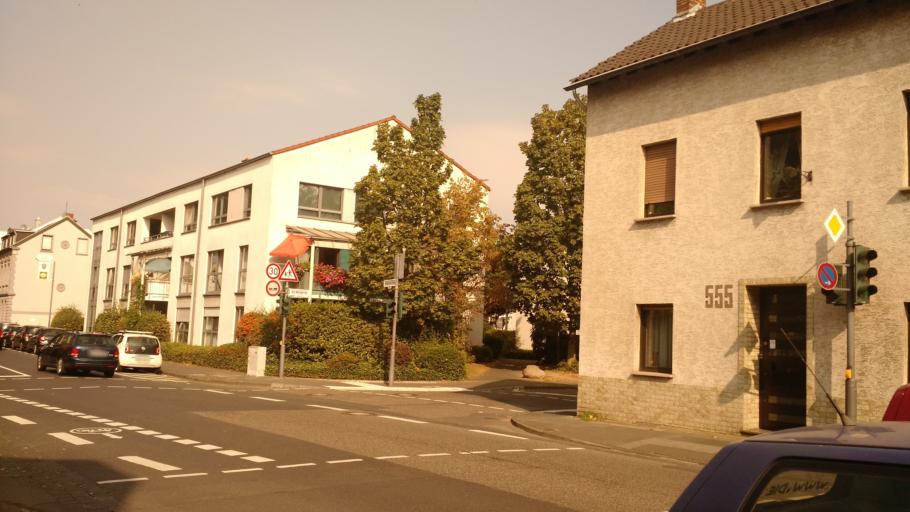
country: DE
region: North Rhine-Westphalia
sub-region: Regierungsbezirk Koln
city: Konigswinter
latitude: 50.7176
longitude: 7.1600
